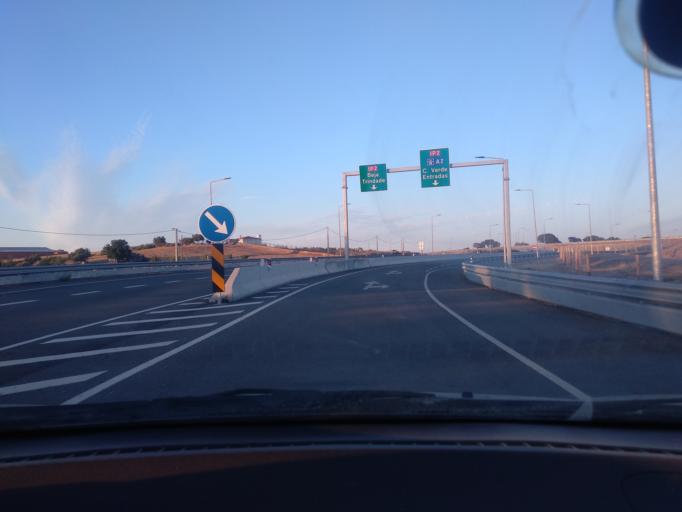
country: PT
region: Beja
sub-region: Beja
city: Beja
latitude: 37.8643
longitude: -7.9549
